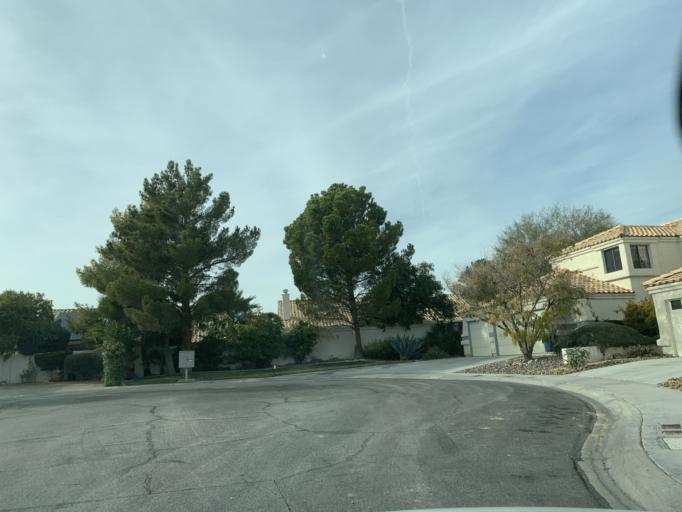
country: US
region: Nevada
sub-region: Clark County
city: Summerlin South
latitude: 36.1347
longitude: -115.3039
